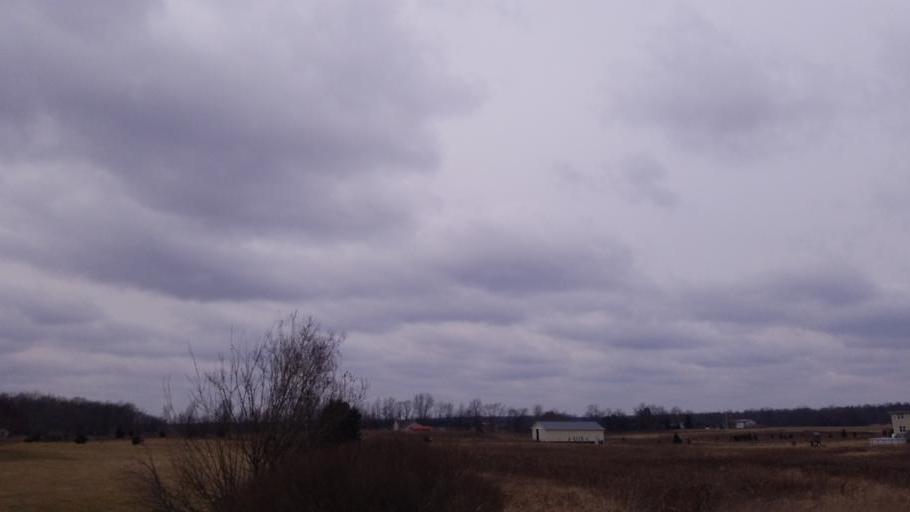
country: US
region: Ohio
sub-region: Crawford County
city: Crestline
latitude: 40.7305
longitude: -82.7031
